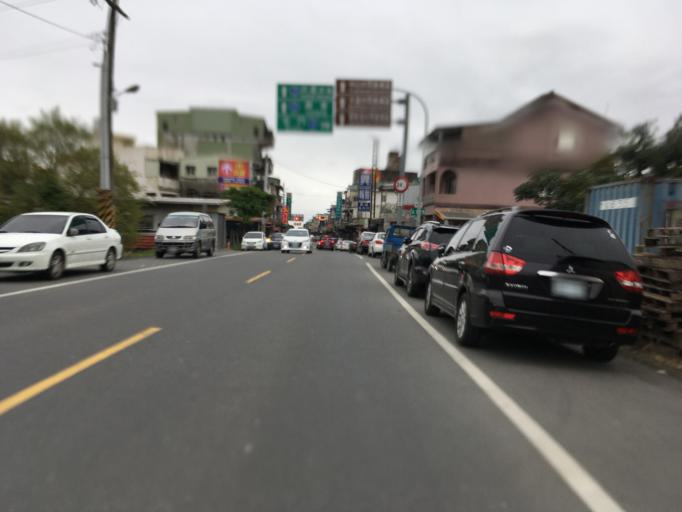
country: TW
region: Taiwan
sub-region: Yilan
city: Yilan
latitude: 24.6617
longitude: 121.6202
